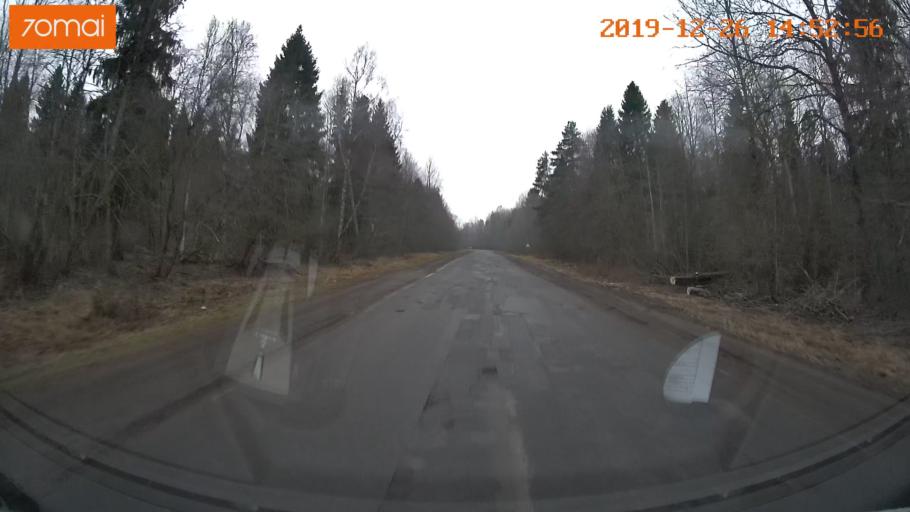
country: RU
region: Jaroslavl
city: Rybinsk
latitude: 58.3185
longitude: 38.8937
